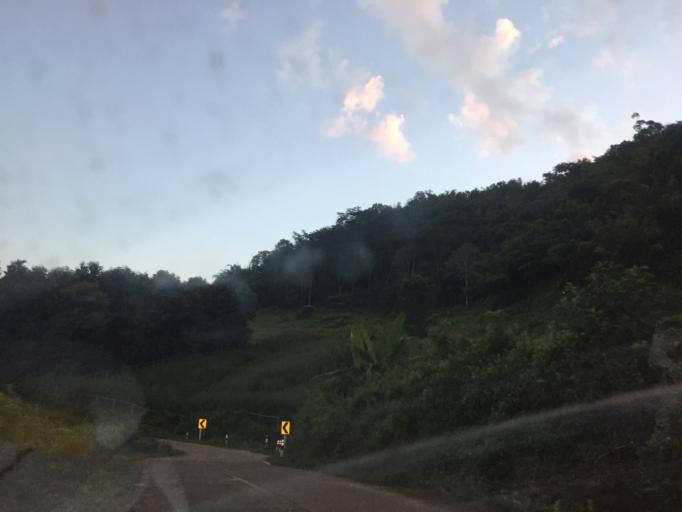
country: TH
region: Chiang Mai
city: Samoeng
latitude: 18.9998
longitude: 98.7151
